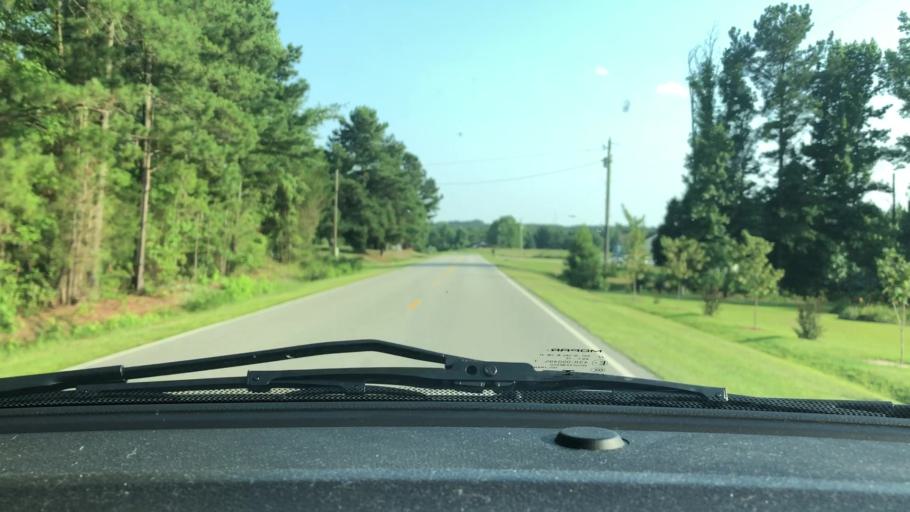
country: US
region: North Carolina
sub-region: Lee County
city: Broadway
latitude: 35.3397
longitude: -79.0728
